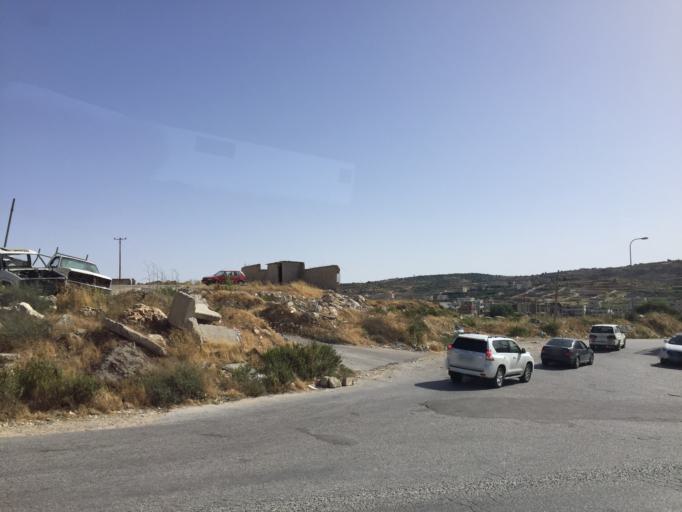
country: PS
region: West Bank
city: Al Khadir
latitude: 31.7043
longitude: 35.1691
